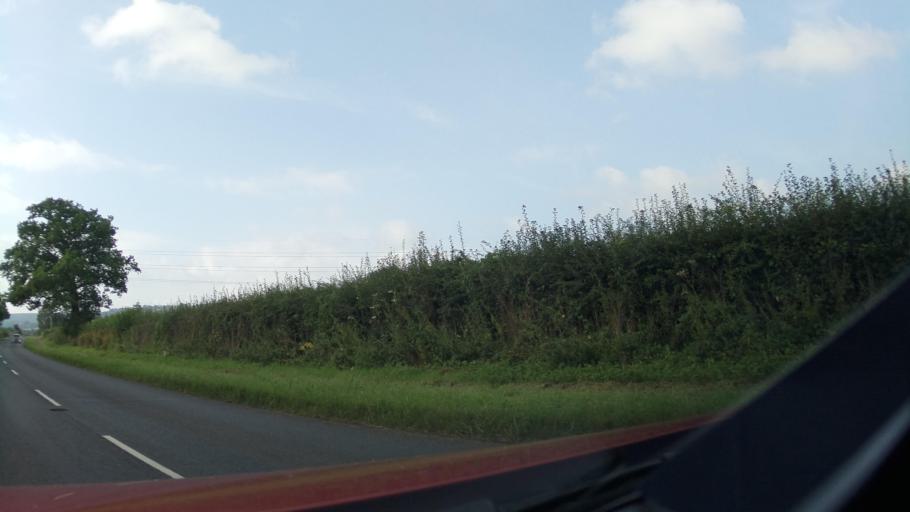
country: GB
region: England
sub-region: Bath and North East Somerset
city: Compton Martin
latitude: 51.3267
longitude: -2.6408
